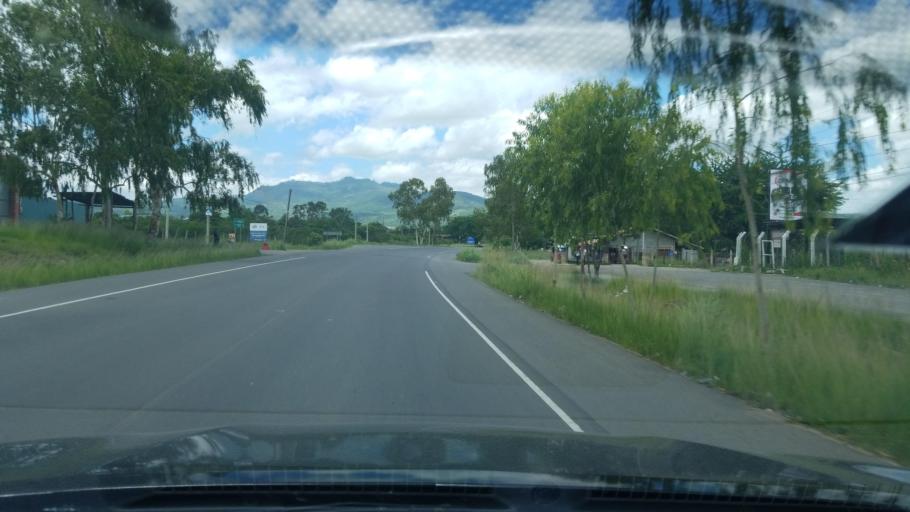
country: HN
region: Francisco Morazan
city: Cofradia
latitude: 14.2871
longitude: -87.2429
